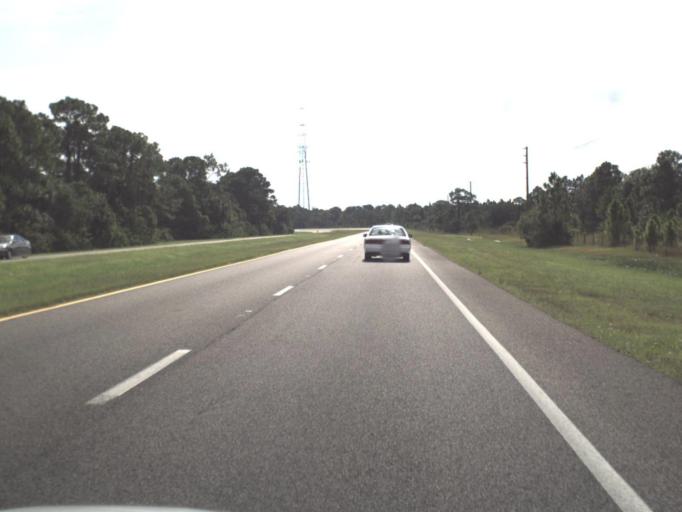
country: US
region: Florida
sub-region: Sarasota County
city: Warm Mineral Springs
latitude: 27.0447
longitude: -82.3094
